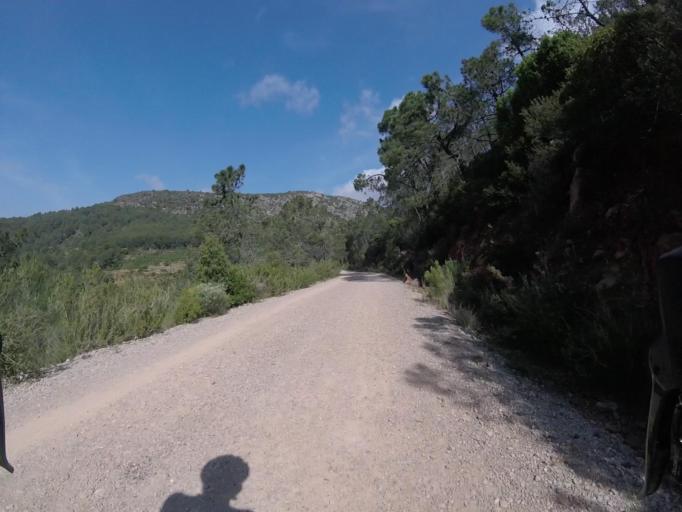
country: ES
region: Valencia
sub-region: Provincia de Castello
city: Cabanes
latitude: 40.0986
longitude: 0.0344
